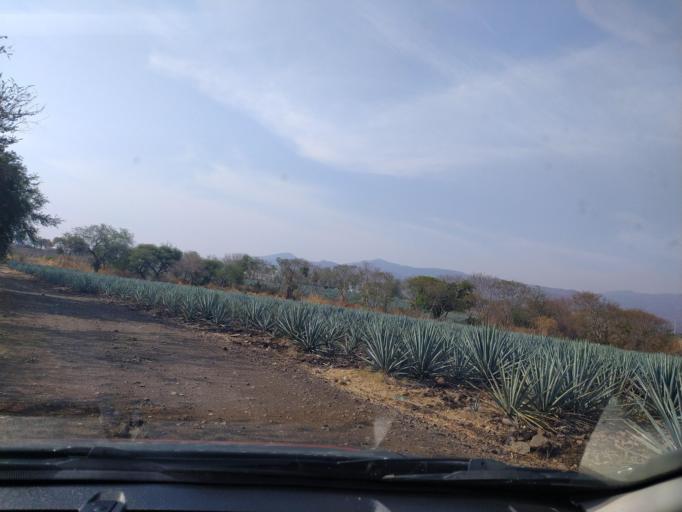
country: MX
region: Jalisco
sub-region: Zacoalco de Torres
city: Barranca de Otates (Barranca de Otatan)
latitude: 20.2734
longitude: -103.6302
